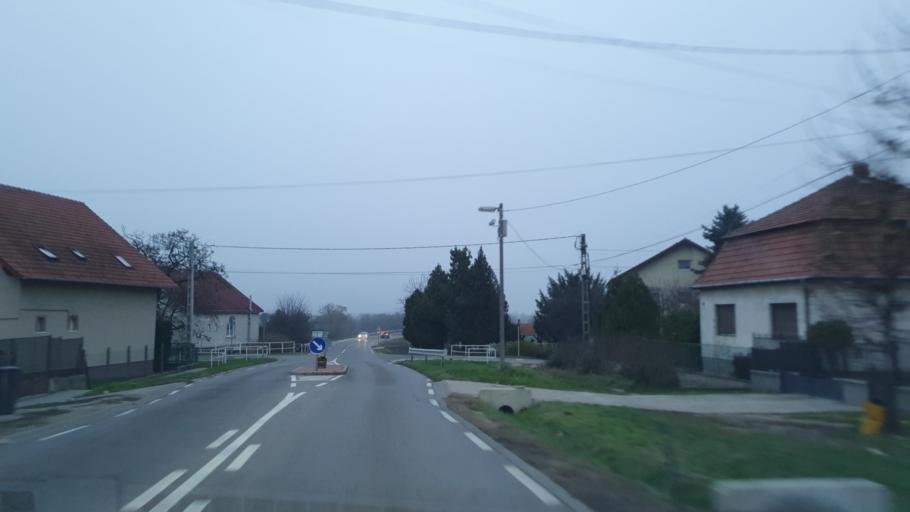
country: HU
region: Pest
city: Csomor
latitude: 47.5386
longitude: 19.2235
